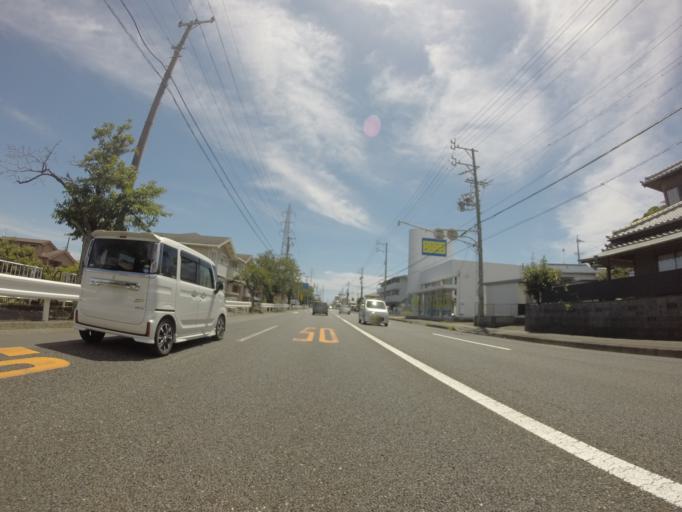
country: JP
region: Shizuoka
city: Shizuoka-shi
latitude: 34.9916
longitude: 138.4850
